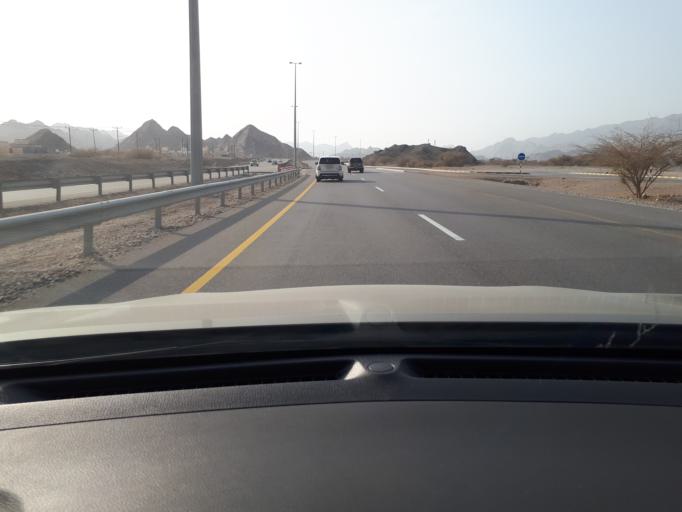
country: OM
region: Muhafazat Masqat
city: Muscat
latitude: 23.2851
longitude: 58.7473
